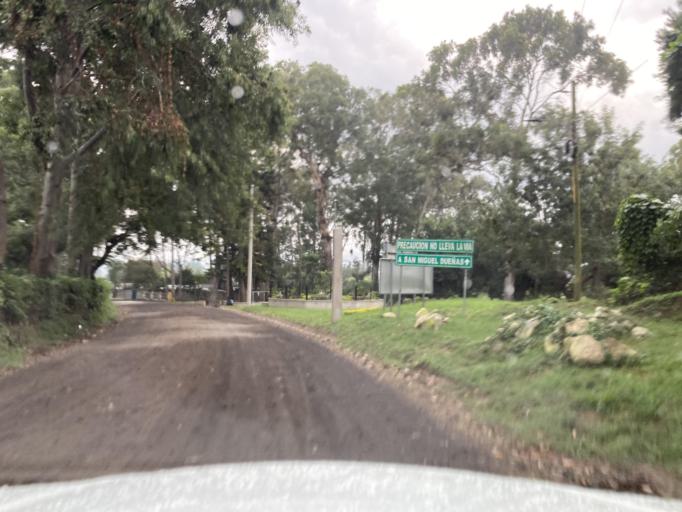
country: GT
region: Sacatepequez
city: San Miguel Duenas
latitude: 14.5231
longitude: -90.8106
